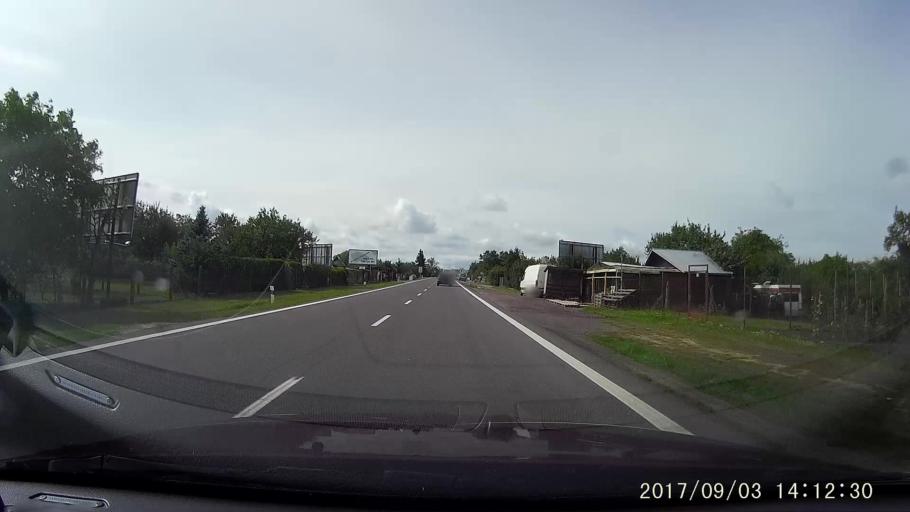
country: CZ
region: South Moravian
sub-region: Okres Znojmo
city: Znojmo
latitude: 48.8717
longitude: 16.0268
